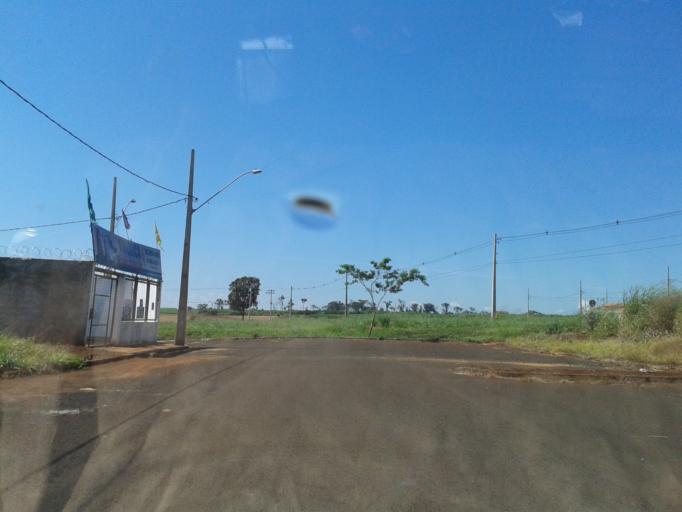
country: BR
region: Goias
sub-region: Itumbiara
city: Itumbiara
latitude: -18.4265
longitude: -49.1829
